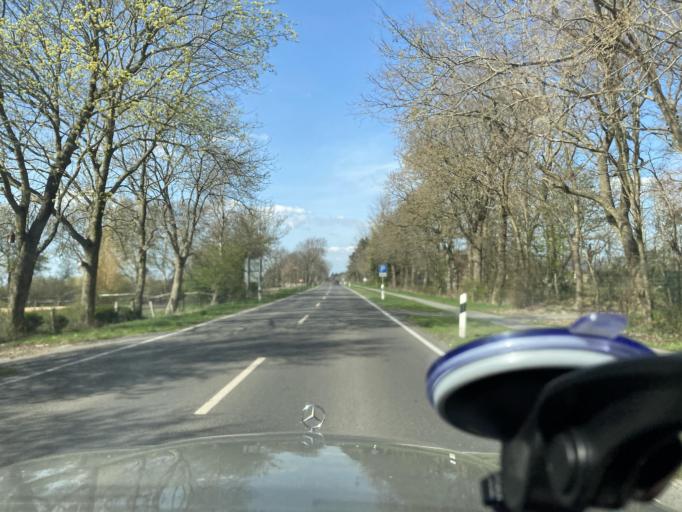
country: DE
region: Schleswig-Holstein
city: Stelle-Wittenwurth
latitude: 54.2834
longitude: 9.0449
